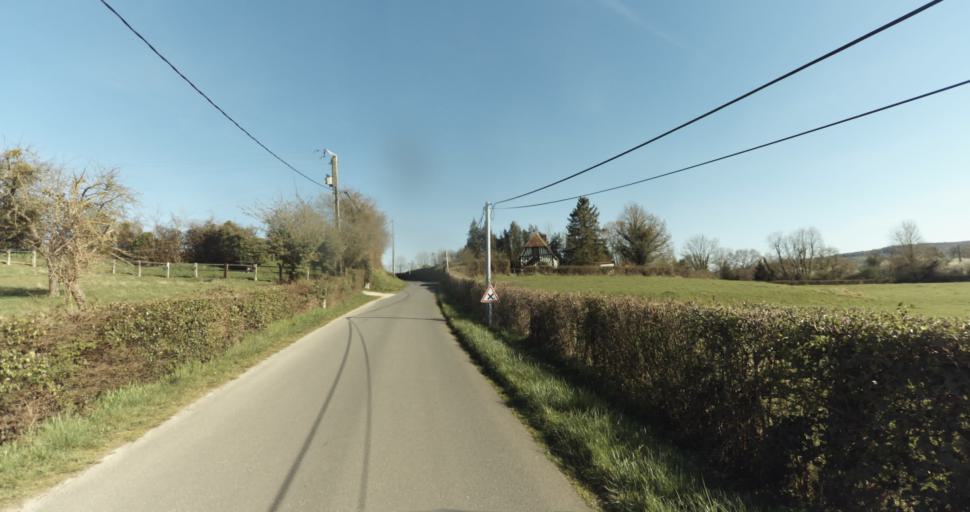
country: FR
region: Lower Normandy
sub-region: Departement du Calvados
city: Saint-Pierre-sur-Dives
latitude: 49.0378
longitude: 0.0446
